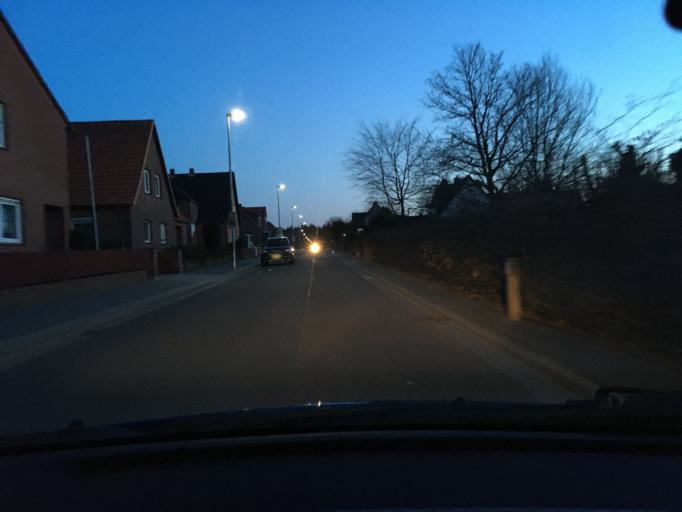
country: DE
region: Lower Saxony
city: Barum
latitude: 52.9956
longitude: 10.5085
